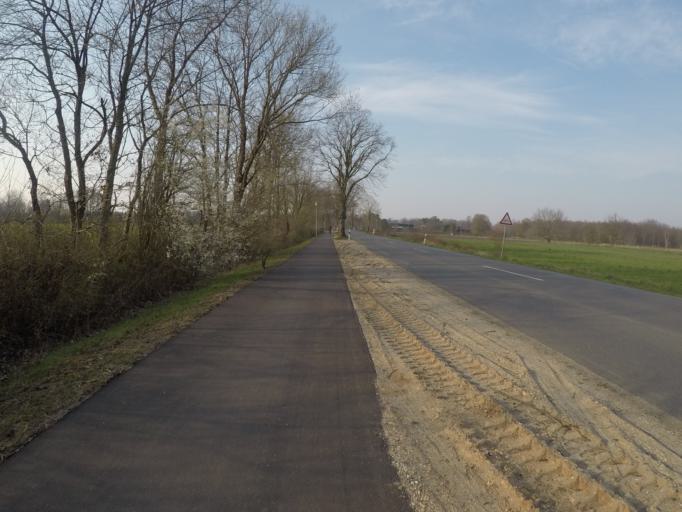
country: DE
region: Schleswig-Holstein
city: Rickling
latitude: 53.9927
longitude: 10.1741
